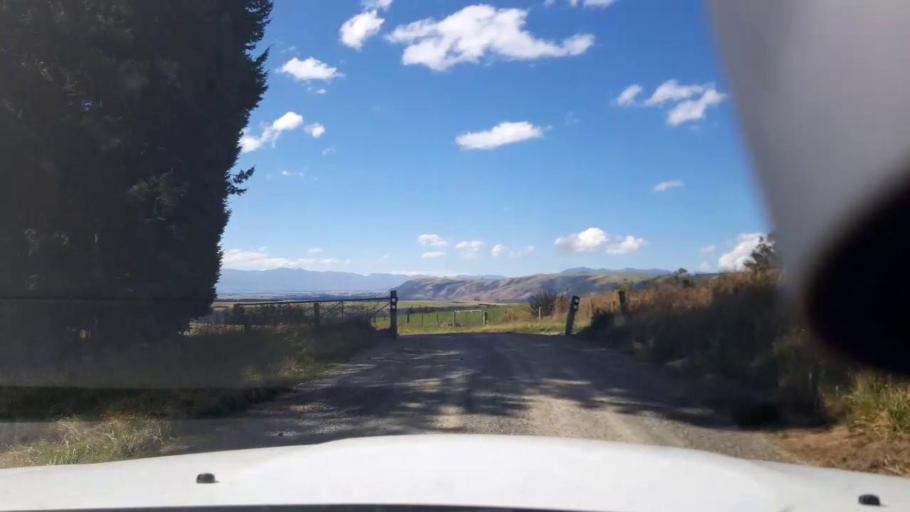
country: NZ
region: Canterbury
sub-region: Timaru District
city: Pleasant Point
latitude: -44.3150
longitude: 170.8755
